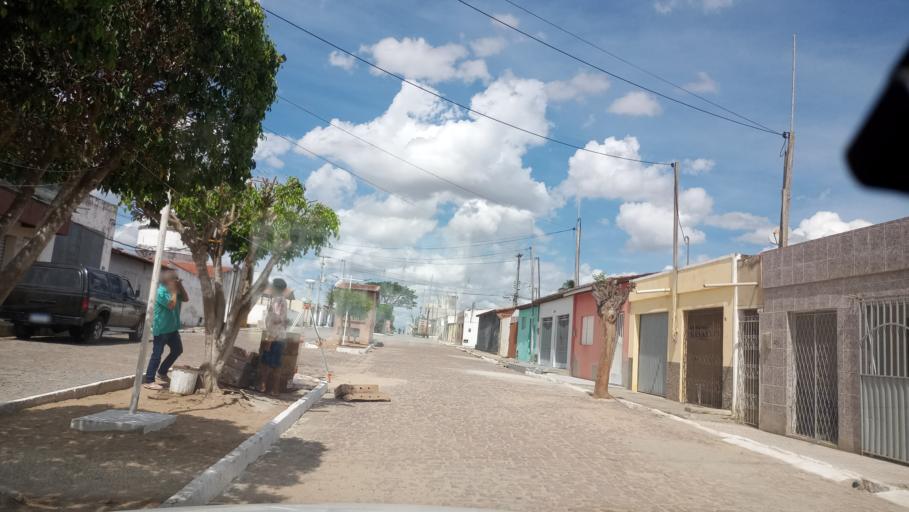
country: BR
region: Rio Grande do Norte
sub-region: Tangara
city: Tangara
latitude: -6.2039
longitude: -35.8042
